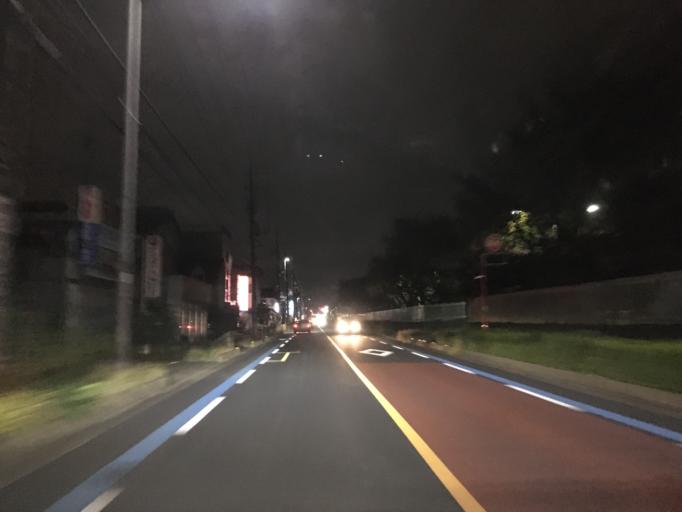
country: JP
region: Saitama
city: Sayama
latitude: 35.8470
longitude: 139.4201
